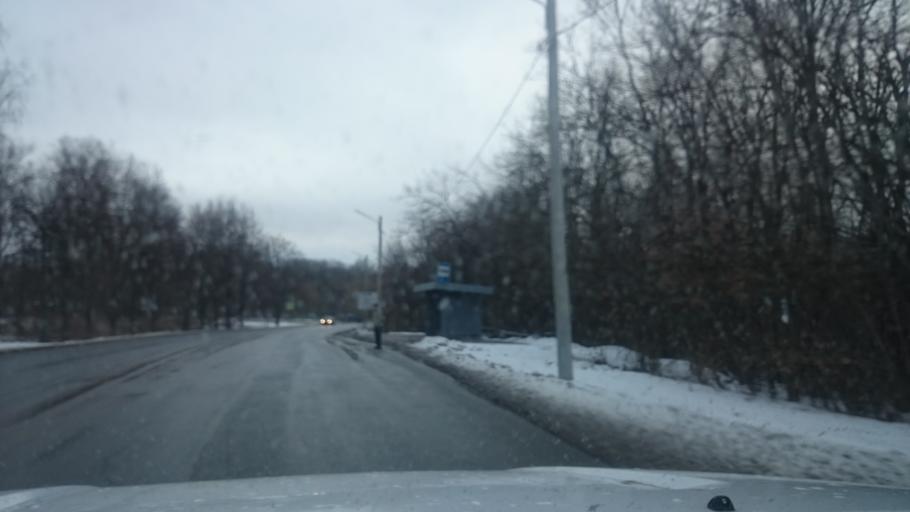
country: RU
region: Tula
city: Mendeleyevskiy
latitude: 54.1199
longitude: 37.5699
